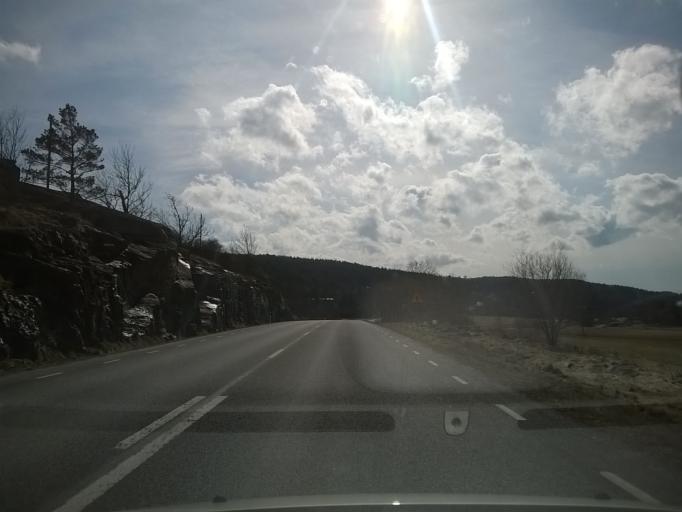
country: SE
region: Vaestra Goetaland
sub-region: Orust
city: Henan
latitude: 58.2760
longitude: 11.6938
